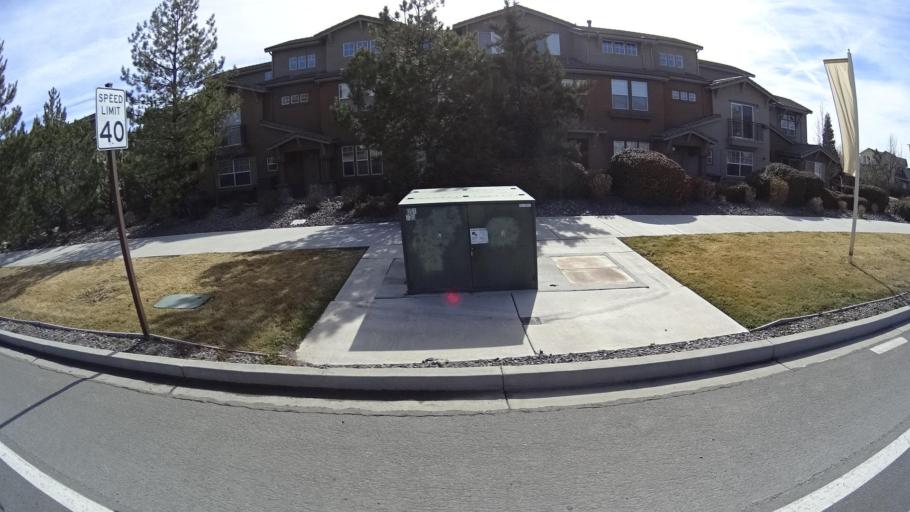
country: US
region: Nevada
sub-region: Washoe County
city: Sun Valley
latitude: 39.5977
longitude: -119.7300
